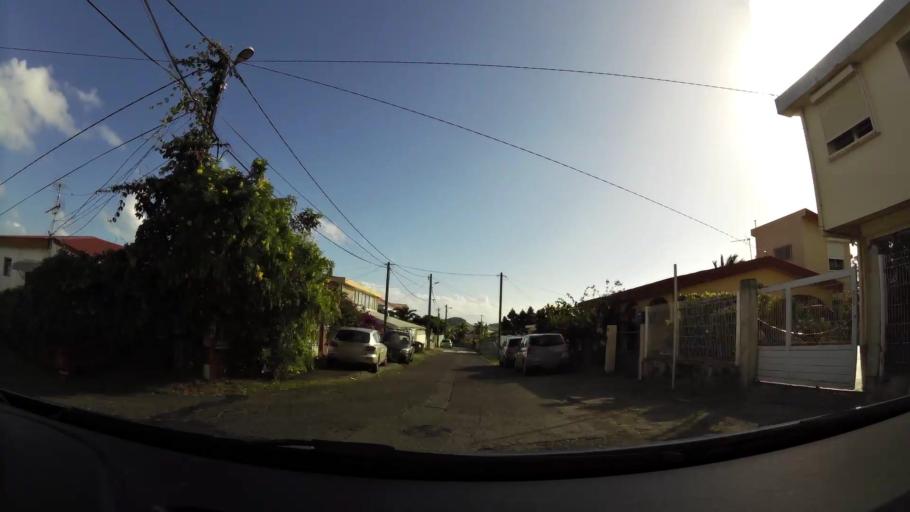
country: MQ
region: Martinique
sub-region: Martinique
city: Le Francois
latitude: 14.6136
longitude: -60.9089
